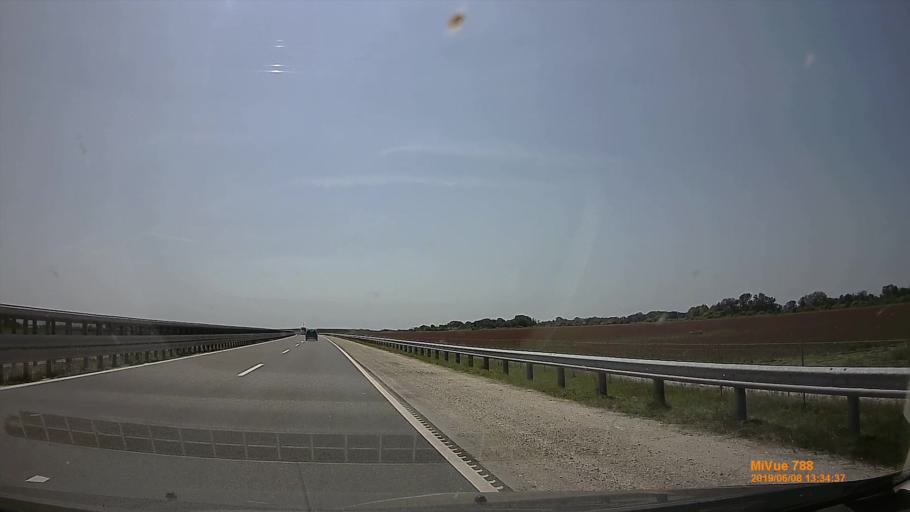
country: HU
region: Gyor-Moson-Sopron
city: Farad
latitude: 47.5442
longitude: 17.2270
